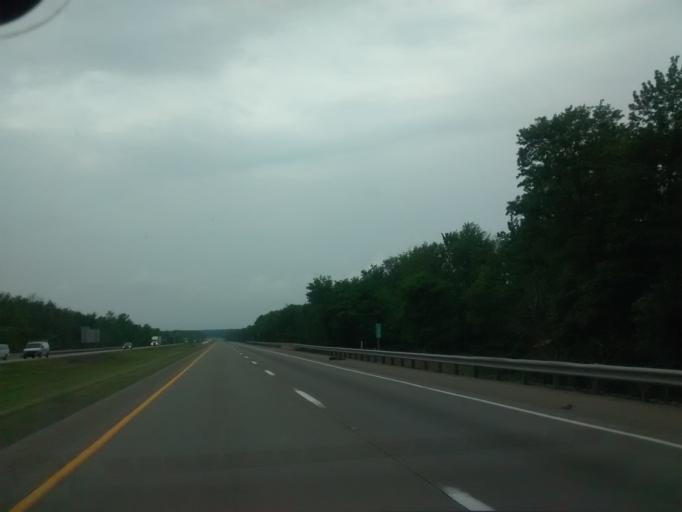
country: US
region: Pennsylvania
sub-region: Monroe County
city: Mount Pocono
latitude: 41.1209
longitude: -75.3993
